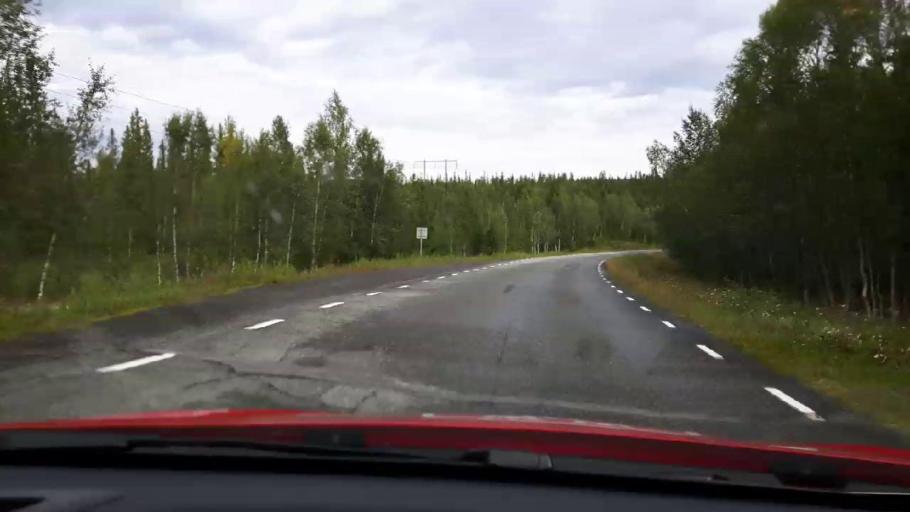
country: SE
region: Jaemtland
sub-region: Are Kommun
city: Are
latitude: 63.7263
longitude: 12.9720
